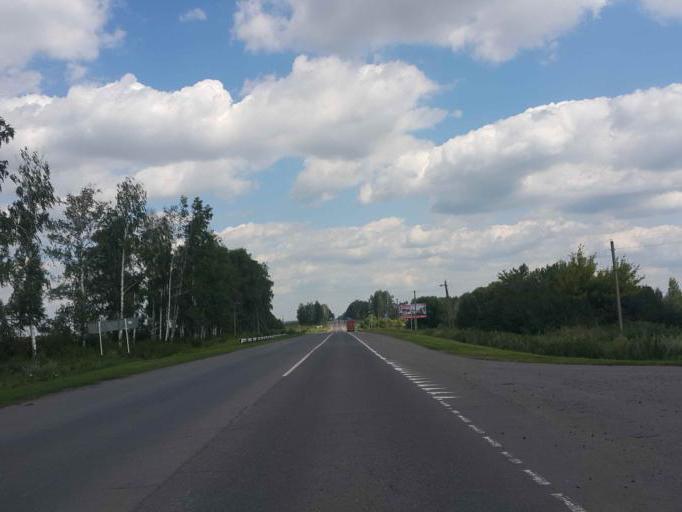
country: RU
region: Tambov
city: Goreloye
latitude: 53.0494
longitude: 41.4765
